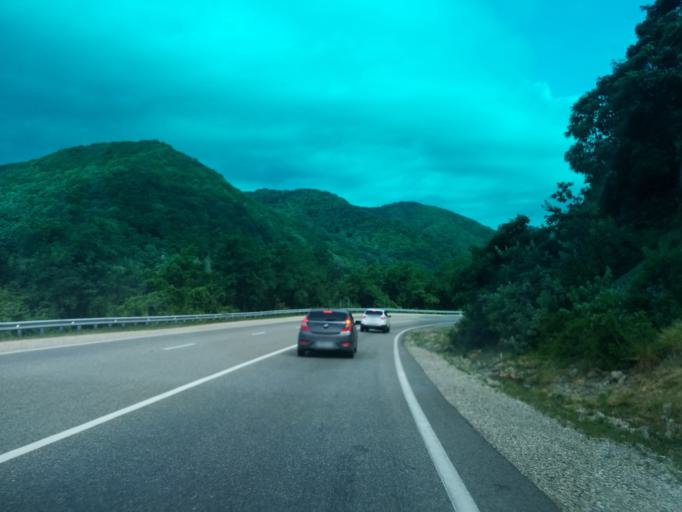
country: RU
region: Krasnodarskiy
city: Nebug
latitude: 44.1721
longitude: 38.9759
